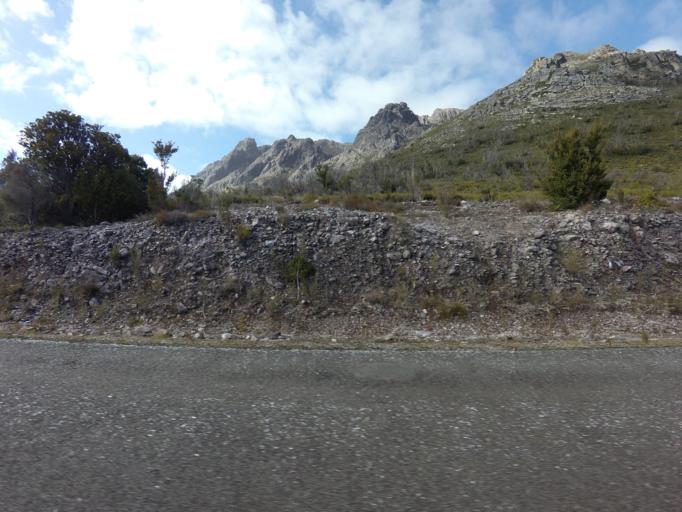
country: AU
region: Tasmania
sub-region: Huon Valley
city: Geeveston
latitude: -42.8612
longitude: 146.2242
